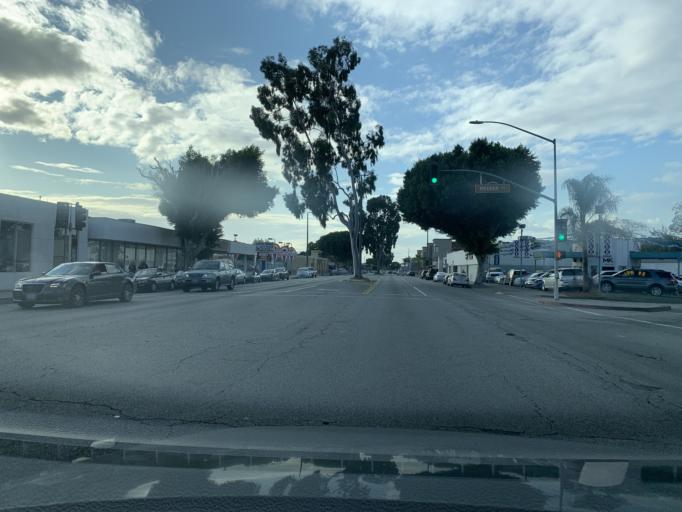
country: US
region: California
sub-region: Los Angeles County
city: El Monte
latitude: 34.0629
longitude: -118.0266
